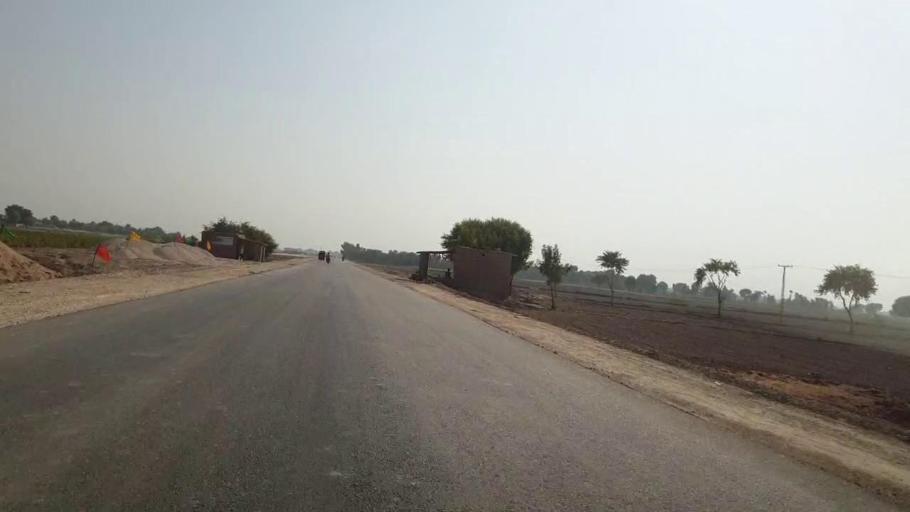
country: PK
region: Sindh
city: Dadu
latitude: 26.6535
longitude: 67.7762
